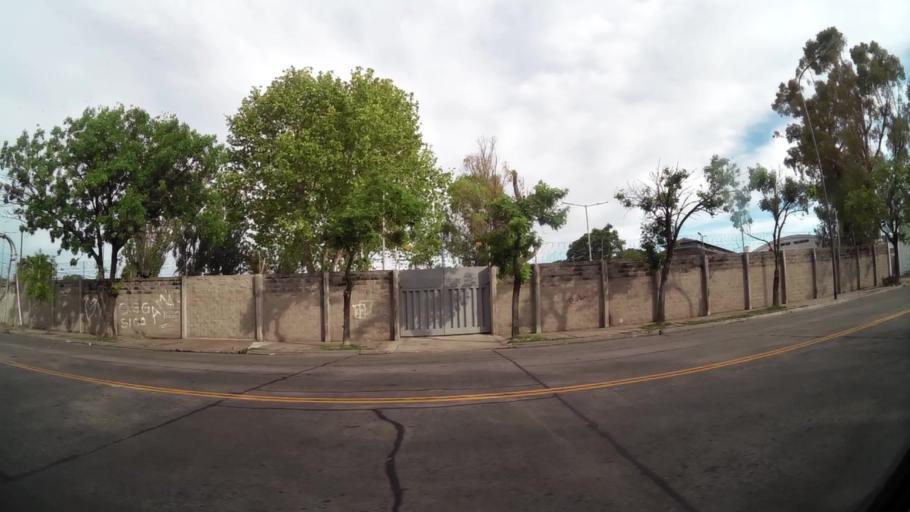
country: AR
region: Buenos Aires F.D.
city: Villa Lugano
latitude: -34.6476
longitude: -58.4497
